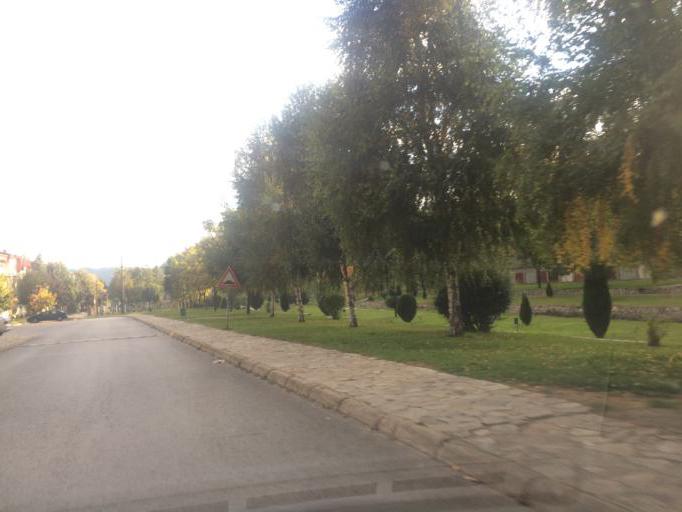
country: MK
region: Makedonska Kamenica
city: Makedonska Kamenica
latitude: 42.0219
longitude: 22.5877
